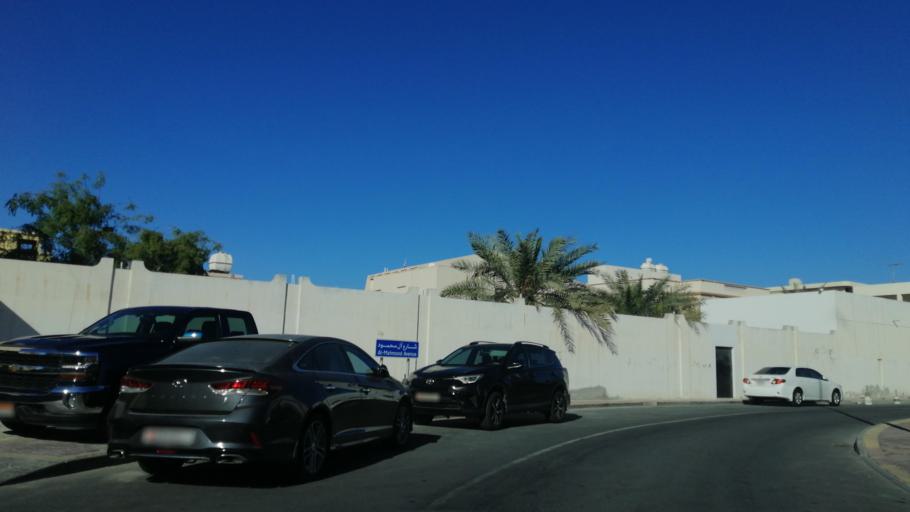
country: BH
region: Muharraq
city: Al Hadd
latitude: 26.2471
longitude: 50.6560
